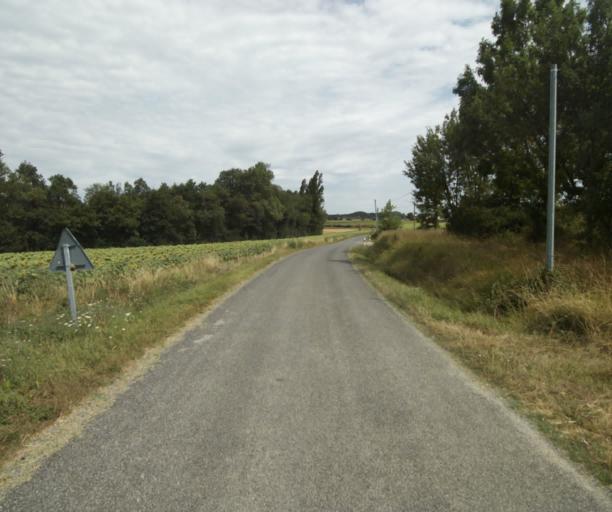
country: FR
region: Midi-Pyrenees
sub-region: Departement de la Haute-Garonne
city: Saint-Felix-Lauragais
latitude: 43.4277
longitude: 1.8984
